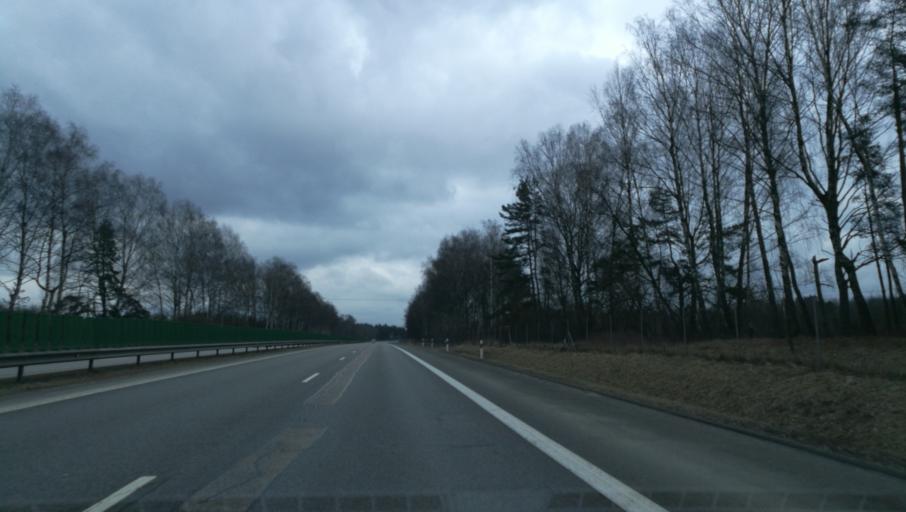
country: LT
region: Vilnius County
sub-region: Vilniaus Rajonas
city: Vievis
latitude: 54.7551
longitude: 24.8964
